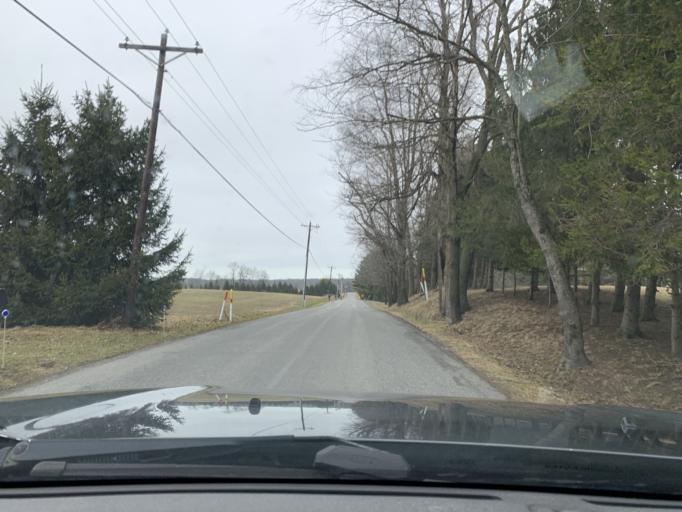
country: US
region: Indiana
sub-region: Porter County
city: Chesterton
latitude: 41.6002
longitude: -86.9899
